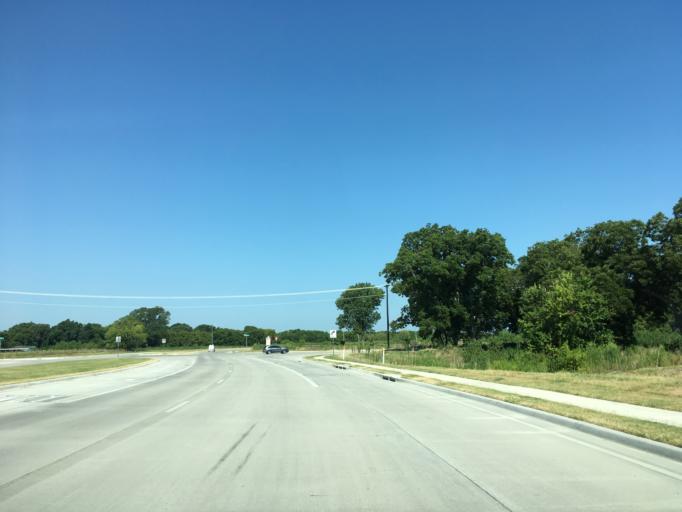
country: US
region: Texas
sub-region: Collin County
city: Fairview
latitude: 33.1660
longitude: -96.5977
